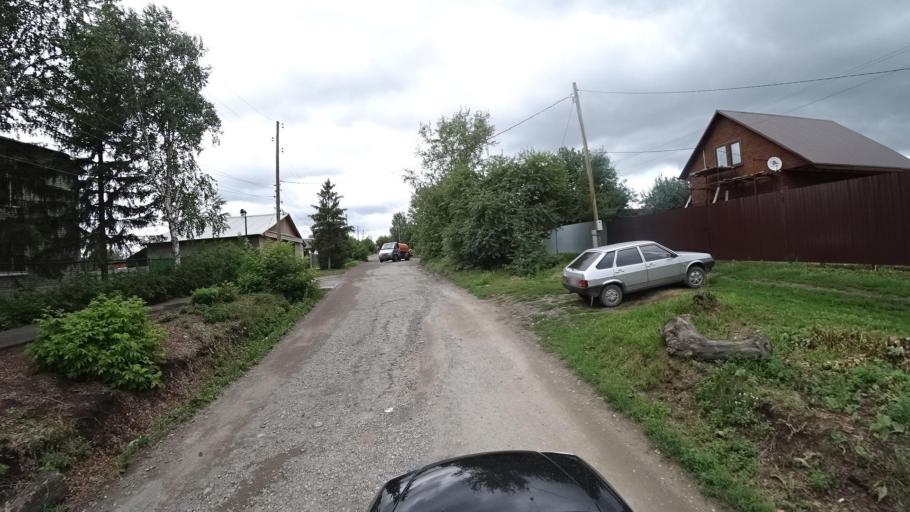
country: RU
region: Sverdlovsk
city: Kamyshlov
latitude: 56.8477
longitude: 62.6812
